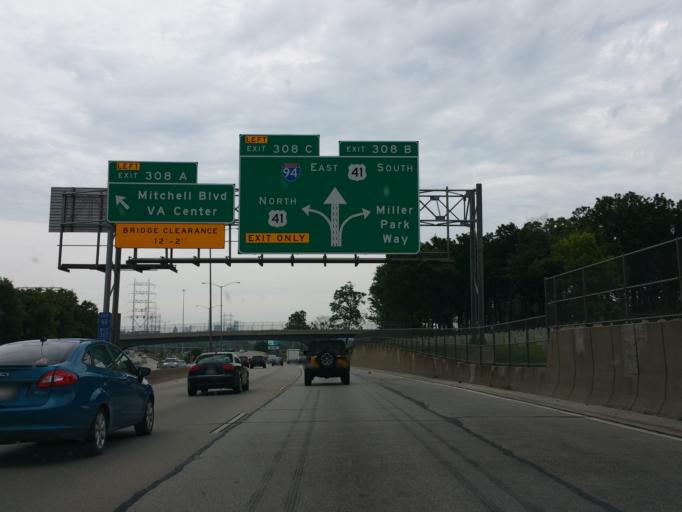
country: US
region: Wisconsin
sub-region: Milwaukee County
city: West Milwaukee
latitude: 43.0304
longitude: -87.9829
